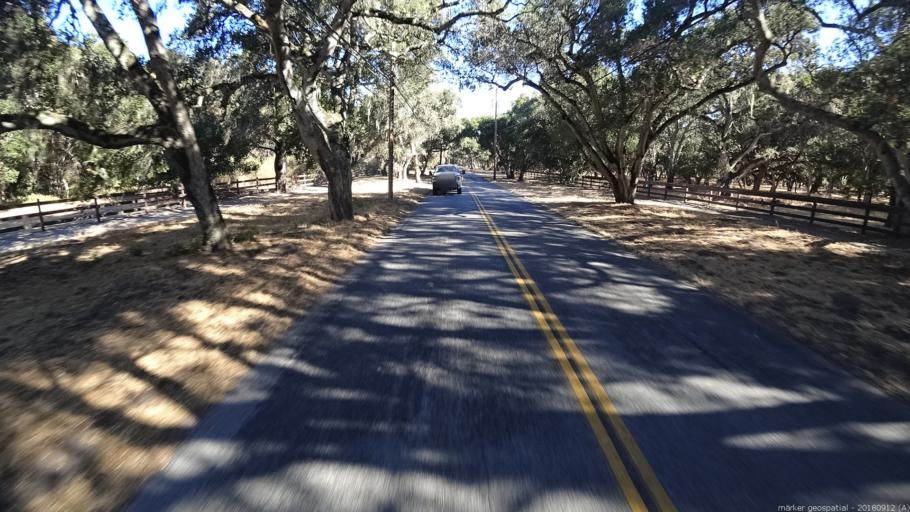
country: US
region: California
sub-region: Monterey County
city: Carmel Valley Village
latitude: 36.5524
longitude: -121.7320
